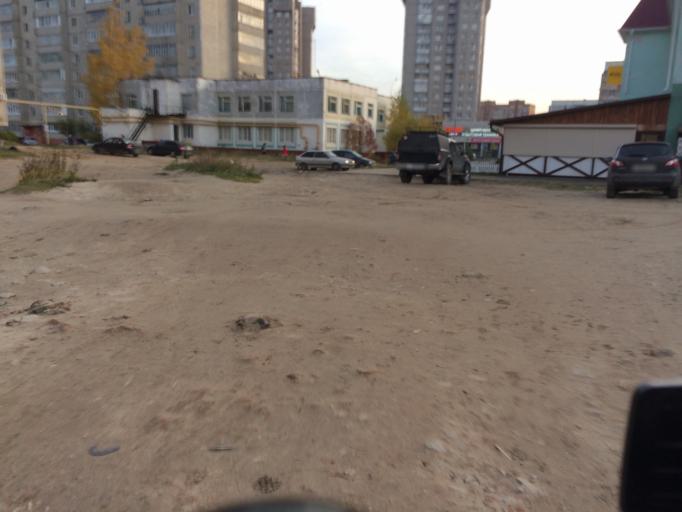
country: RU
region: Mariy-El
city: Yoshkar-Ola
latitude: 56.6356
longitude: 47.9268
